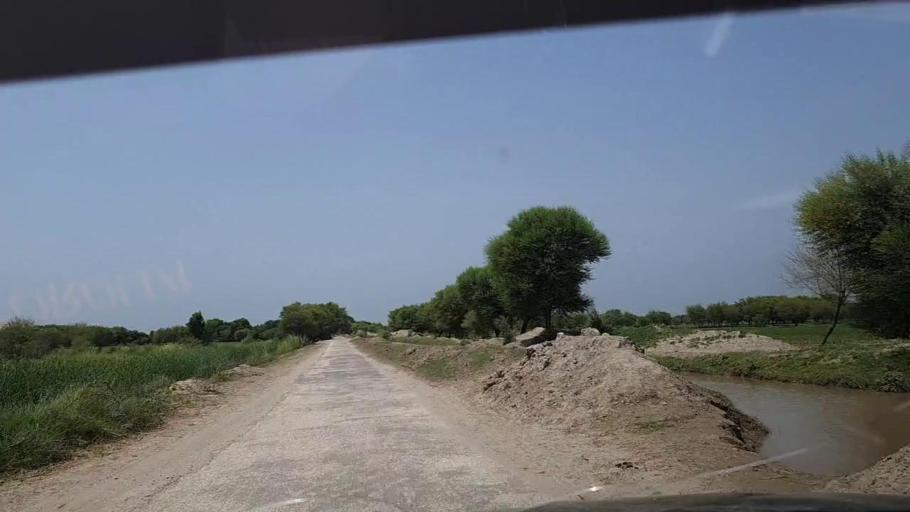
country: PK
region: Sindh
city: Khanpur
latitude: 27.8145
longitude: 69.4500
